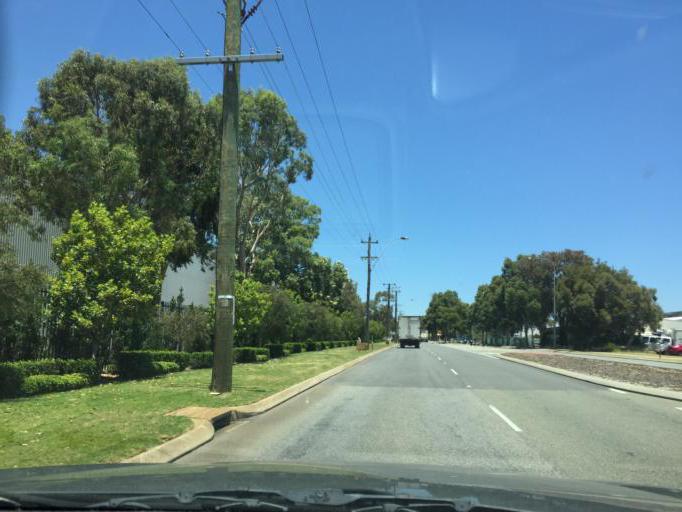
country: AU
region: Western Australia
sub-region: Canning
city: Canning Vale
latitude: -32.0603
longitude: 115.9308
